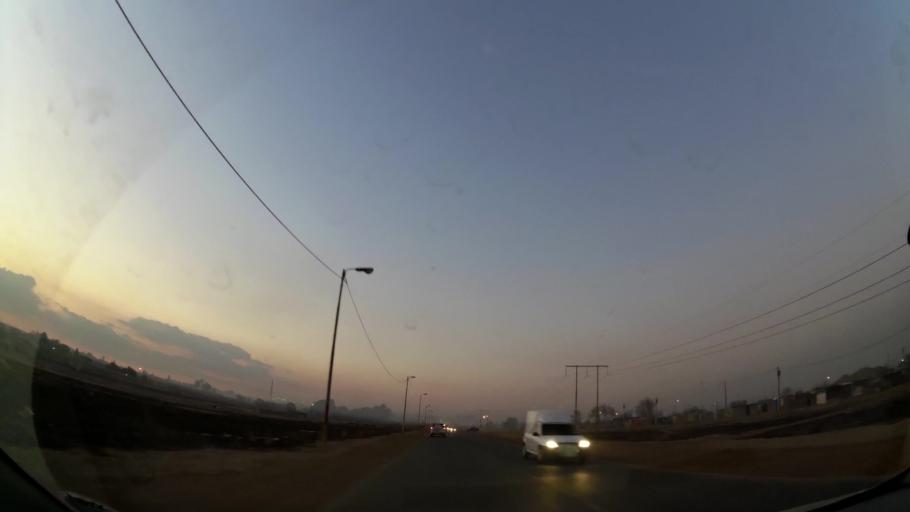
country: ZA
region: Gauteng
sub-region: Ekurhuleni Metropolitan Municipality
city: Springs
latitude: -26.3104
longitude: 28.3787
